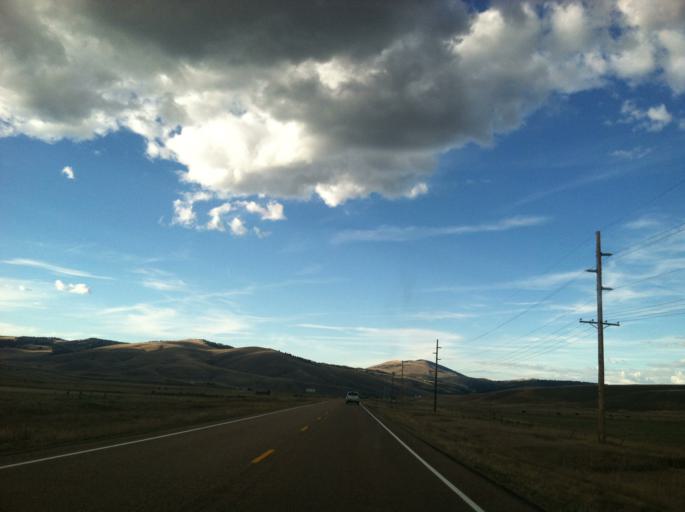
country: US
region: Montana
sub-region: Granite County
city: Philipsburg
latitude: 46.3513
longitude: -113.3137
